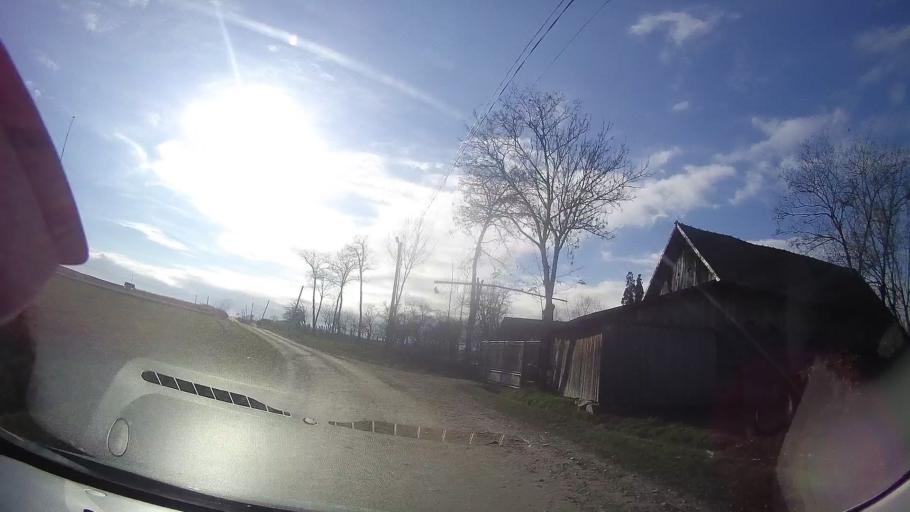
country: RO
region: Mures
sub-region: Comuna Papiu Ilarian
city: Papiu Ilarian
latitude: 46.5688
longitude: 24.2093
